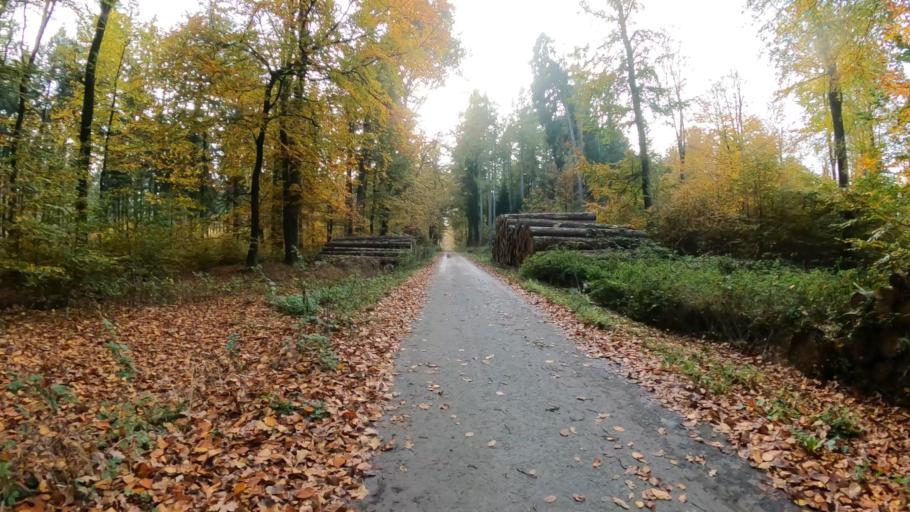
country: DE
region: Lower Saxony
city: Neu Wulmstorf
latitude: 53.3981
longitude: 9.8350
